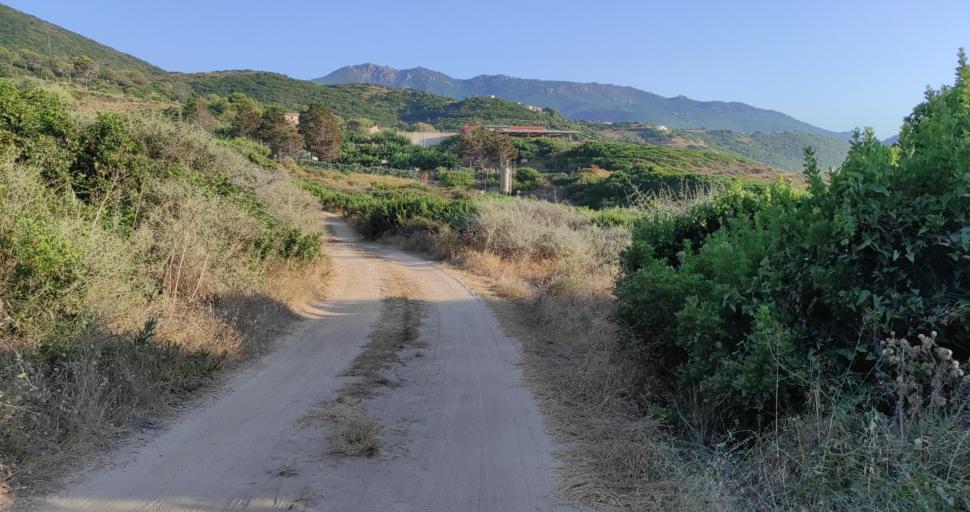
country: FR
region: Corsica
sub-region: Departement de la Corse-du-Sud
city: Alata
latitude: 41.9858
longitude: 8.6707
